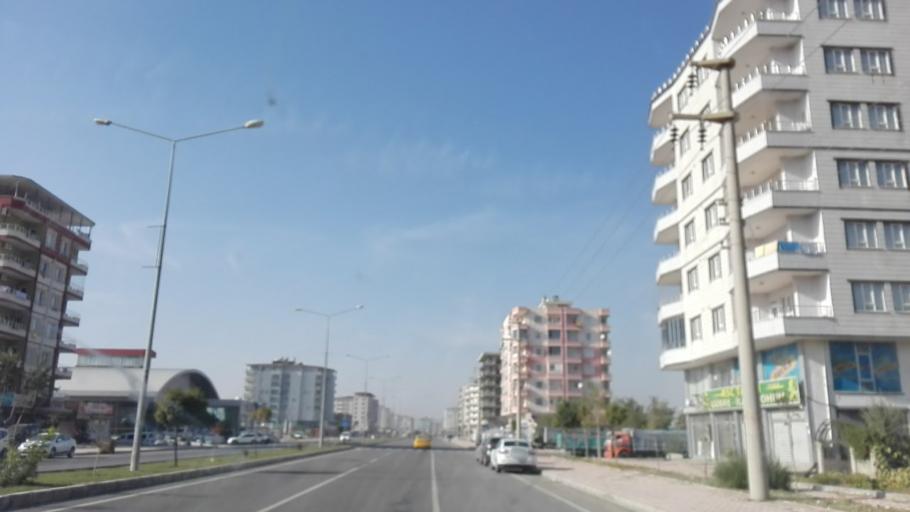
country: TR
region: Batman
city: Aydinkonak
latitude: 37.8854
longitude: 41.1604
